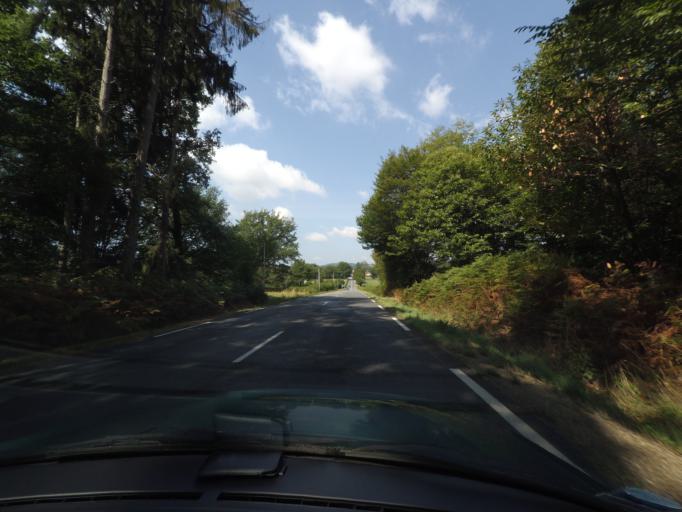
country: FR
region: Limousin
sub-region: Departement de la Haute-Vienne
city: Neuvic-Entier
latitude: 45.7612
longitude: 1.5782
